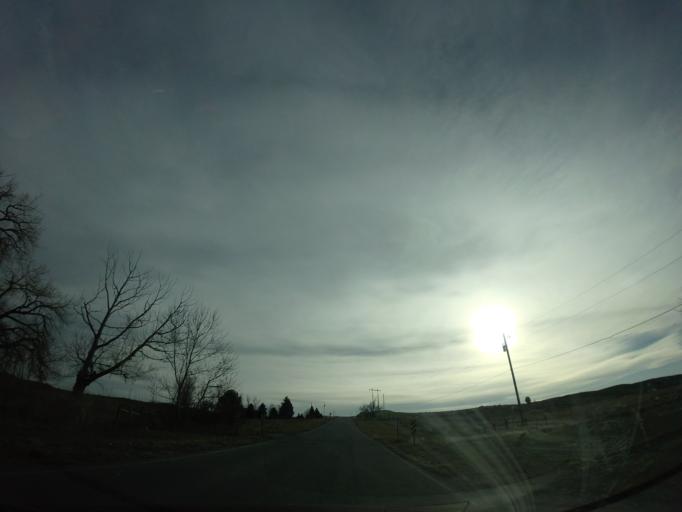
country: US
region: Montana
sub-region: Yellowstone County
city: Billings
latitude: 45.7947
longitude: -108.4556
